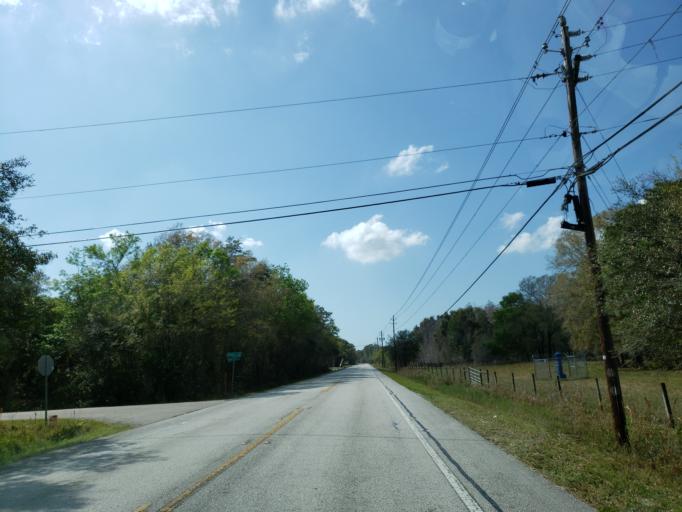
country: US
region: Florida
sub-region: Hillsborough County
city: Keystone
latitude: 28.1429
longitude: -82.6124
